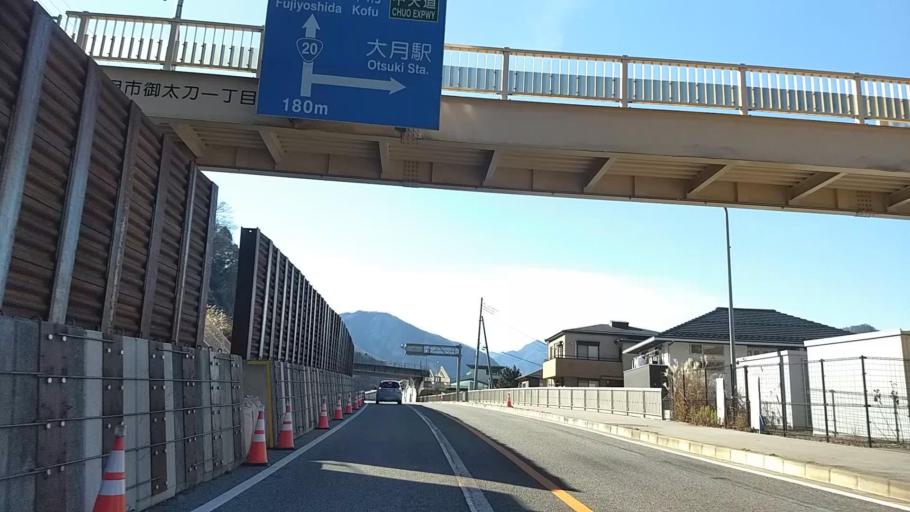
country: JP
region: Yamanashi
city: Otsuki
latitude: 35.6116
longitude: 138.9464
